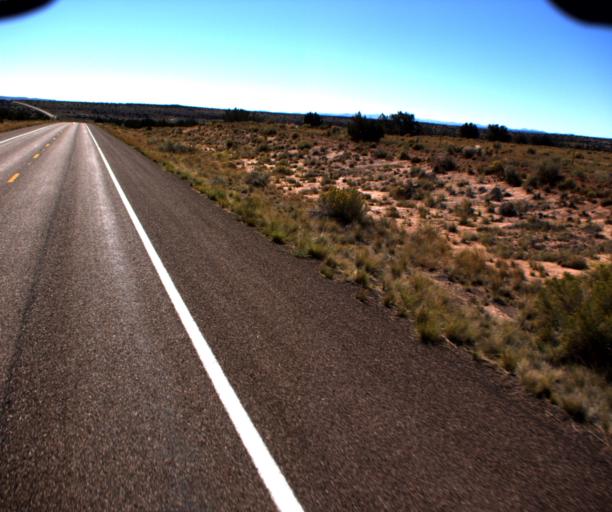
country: US
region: Arizona
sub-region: Apache County
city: Saint Johns
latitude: 34.6558
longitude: -109.7107
